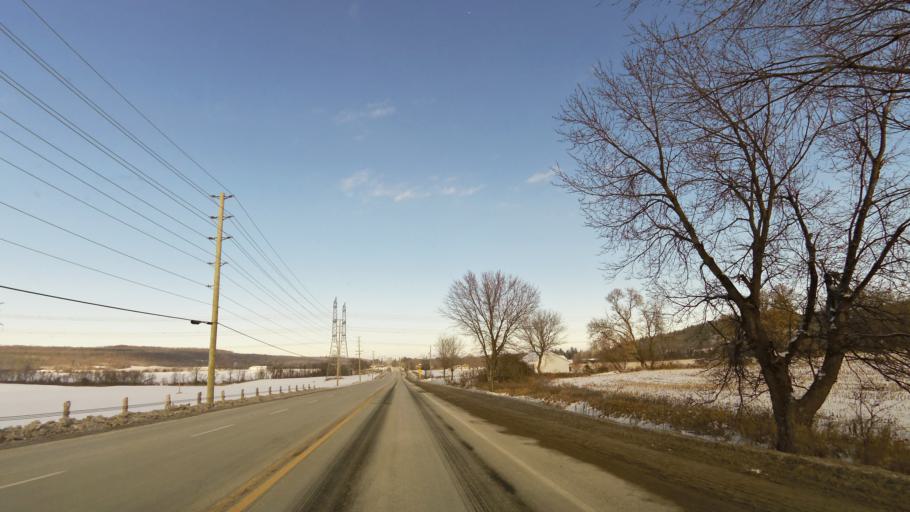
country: CA
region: Ontario
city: Quinte West
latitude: 44.1496
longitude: -77.7952
